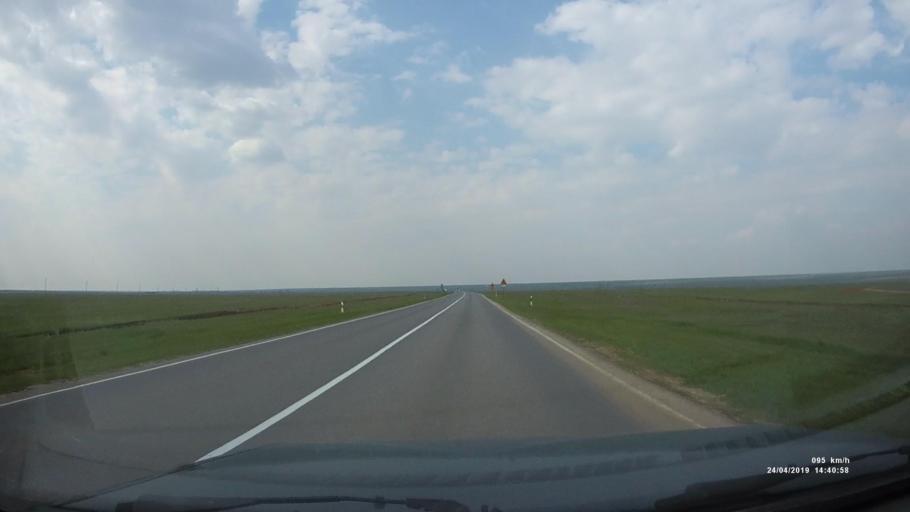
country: RU
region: Rostov
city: Remontnoye
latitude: 46.4395
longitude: 43.8843
